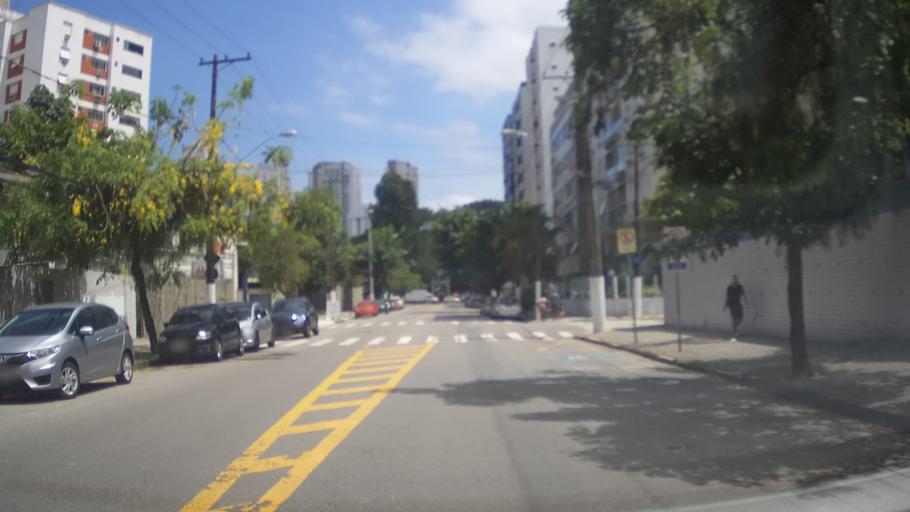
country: BR
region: Sao Paulo
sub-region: Santos
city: Santos
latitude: -23.9649
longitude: -46.3473
